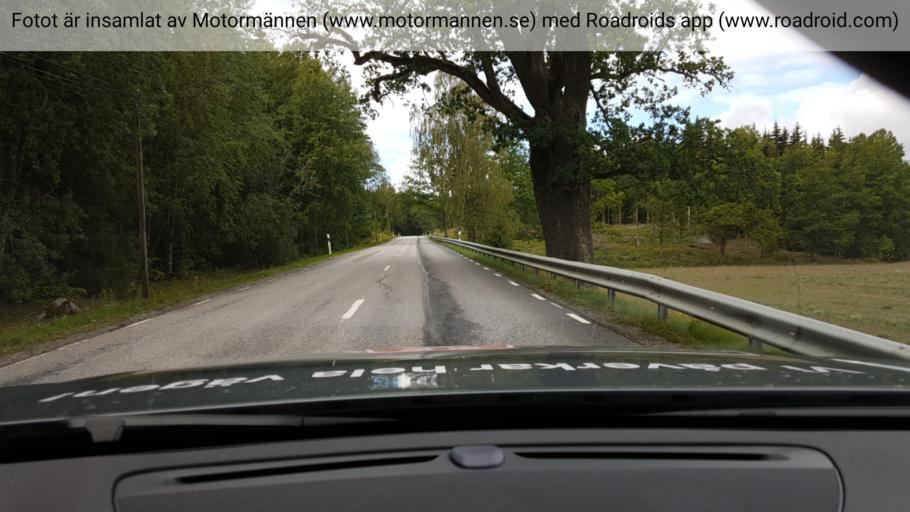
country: SE
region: Stockholm
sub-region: Nykvarns Kommun
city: Nykvarn
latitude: 59.2055
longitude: 17.3949
